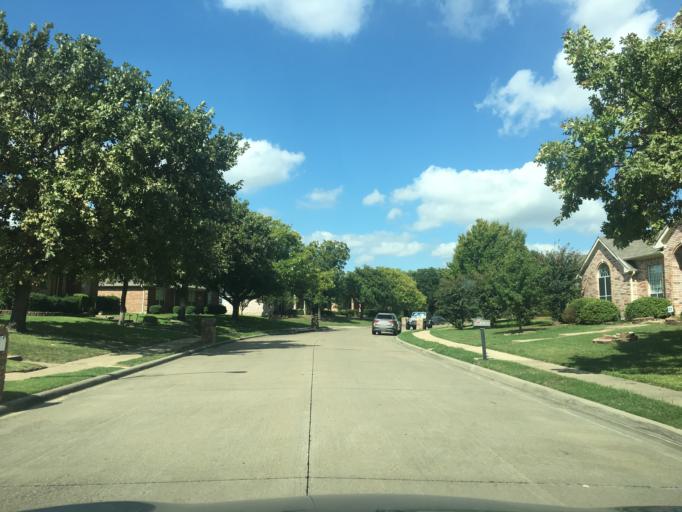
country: US
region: Texas
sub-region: Dallas County
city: Sachse
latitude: 32.9667
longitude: -96.5967
